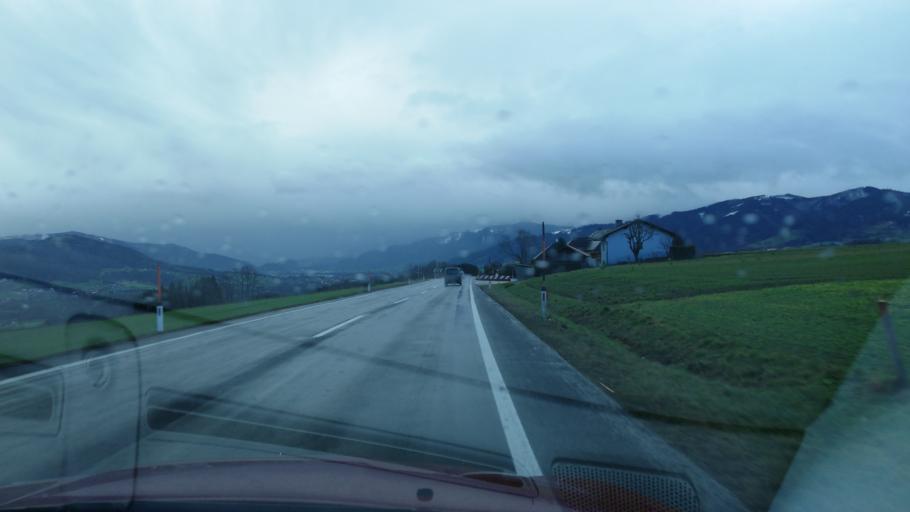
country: AT
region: Upper Austria
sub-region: Politischer Bezirk Kirchdorf an der Krems
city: Kremsmunster
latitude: 47.9692
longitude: 14.0789
